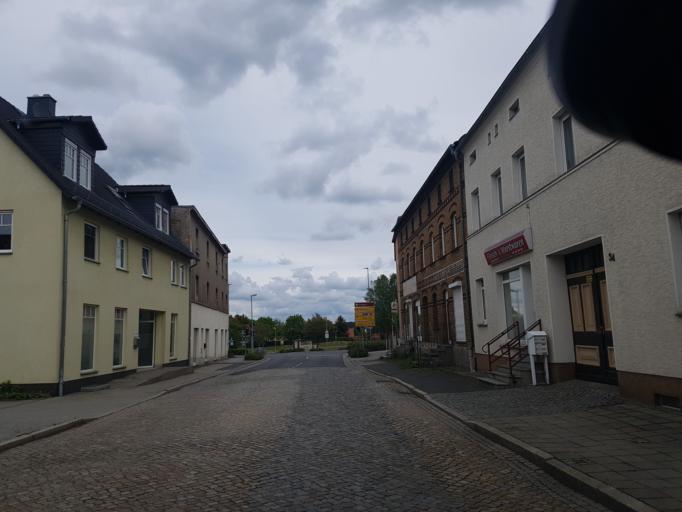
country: DE
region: Brandenburg
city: Tschernitz
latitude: 51.6141
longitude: 14.5969
